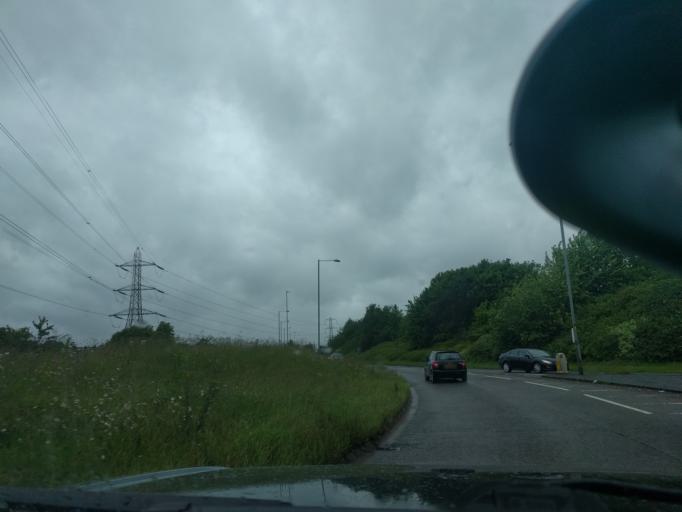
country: GB
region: England
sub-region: Wiltshire
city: Chippenham
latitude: 51.4504
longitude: -2.1517
